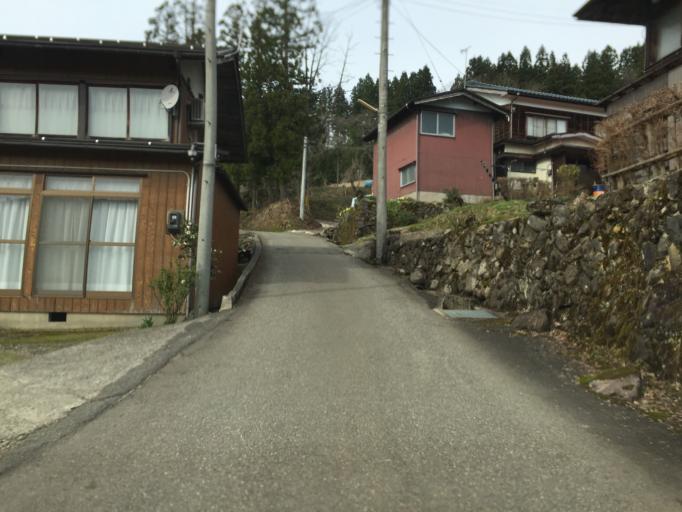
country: JP
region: Niigata
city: Tochio-honcho
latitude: 37.4449
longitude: 139.0309
